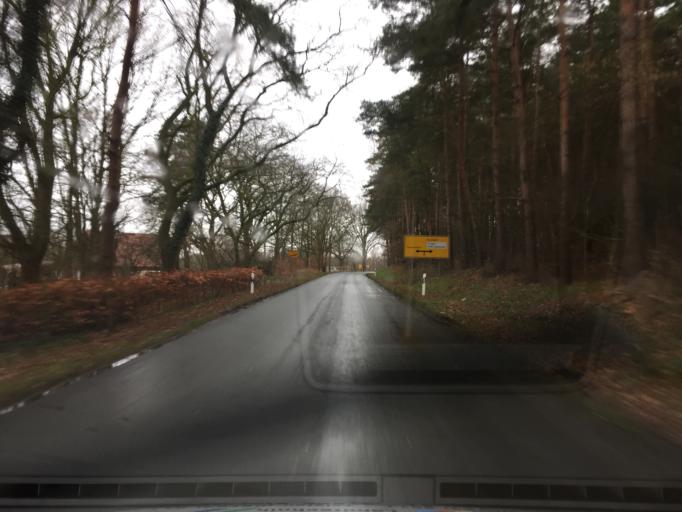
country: DE
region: Lower Saxony
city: Steyerberg
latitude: 52.5709
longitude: 9.0123
